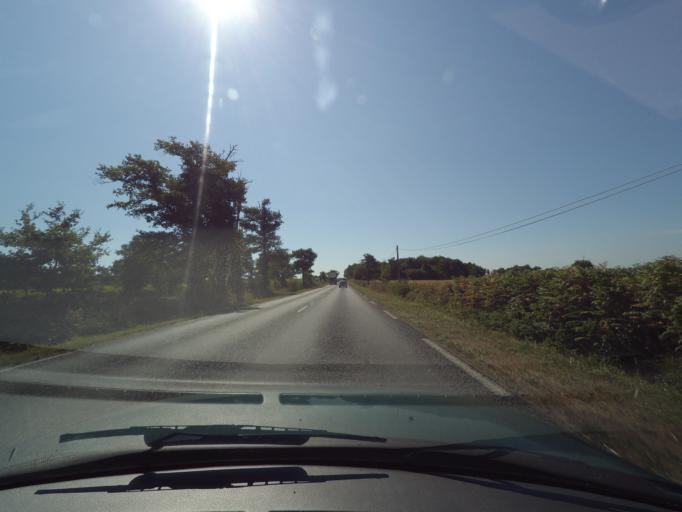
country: FR
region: Limousin
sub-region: Departement de la Haute-Vienne
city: Bellac
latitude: 46.0872
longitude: 1.0835
